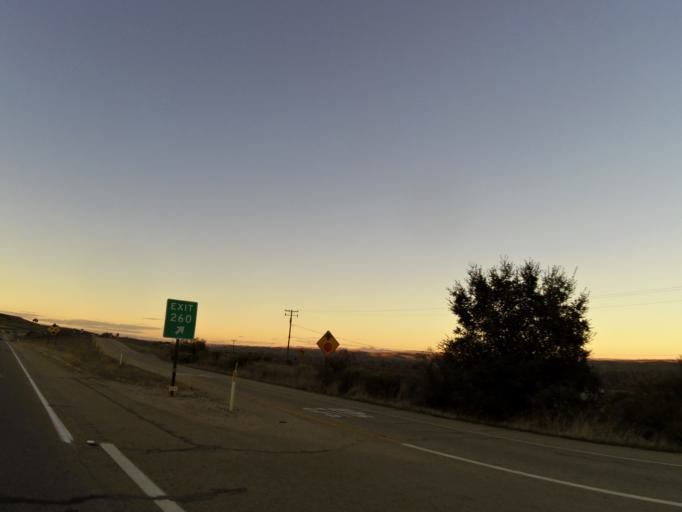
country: US
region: California
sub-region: San Luis Obispo County
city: Lake Nacimiento
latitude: 35.9738
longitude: -120.8981
